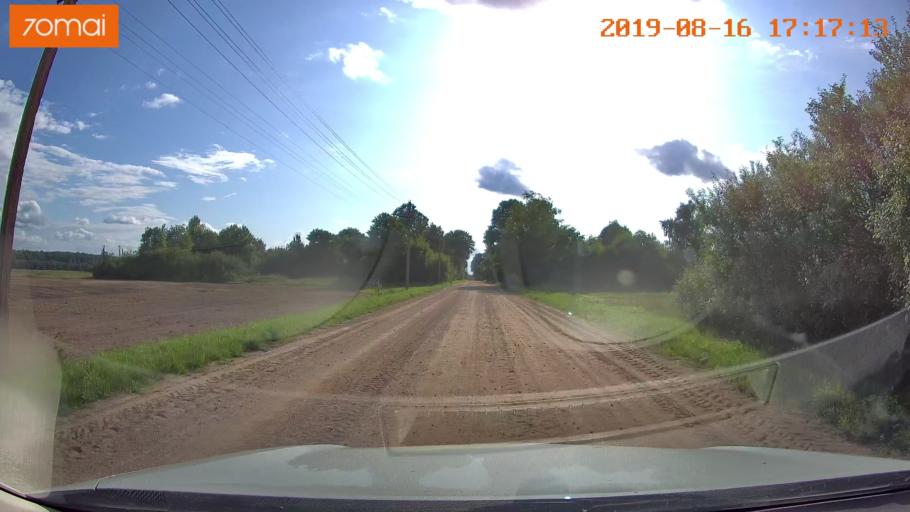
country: BY
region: Mogilev
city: Hlusha
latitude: 53.1722
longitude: 28.8111
